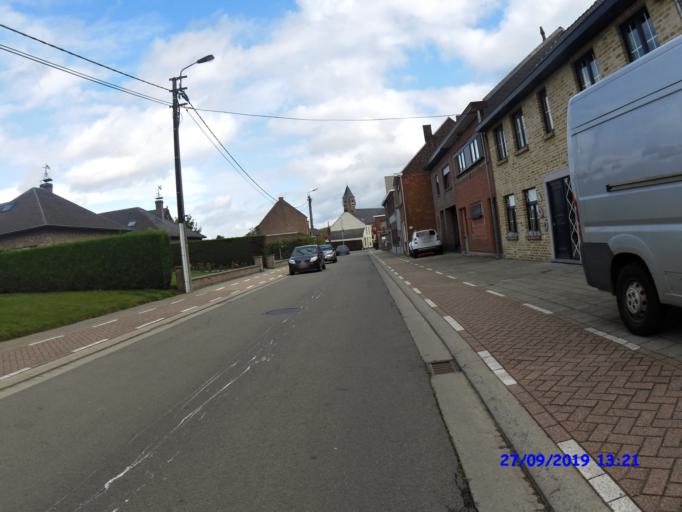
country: BE
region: Flanders
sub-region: Provincie Oost-Vlaanderen
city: Lede
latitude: 50.9591
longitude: 3.9505
